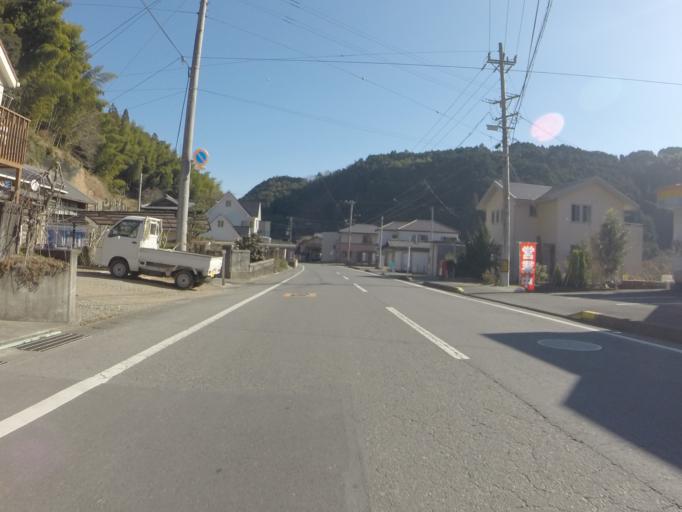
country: JP
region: Shizuoka
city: Shizuoka-shi
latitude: 35.1088
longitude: 138.4649
